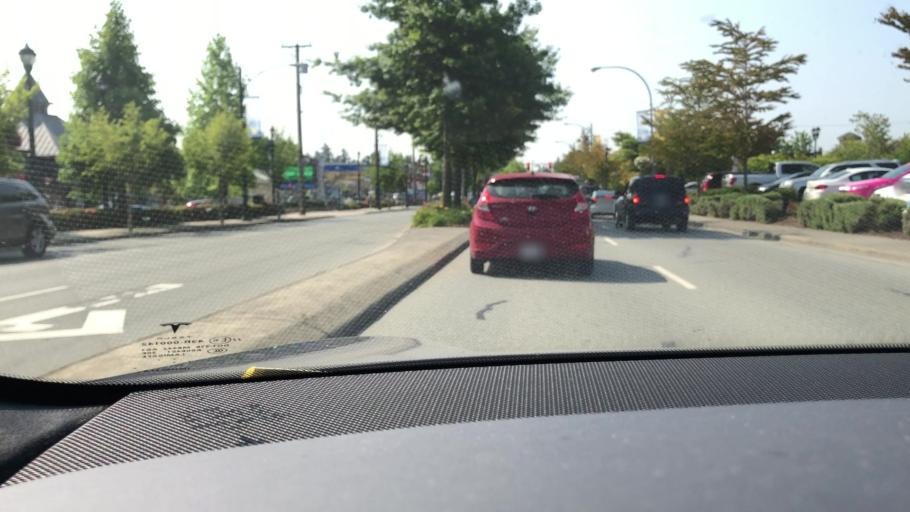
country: US
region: Washington
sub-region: Whatcom County
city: Point Roberts
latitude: 49.0261
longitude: -123.0688
